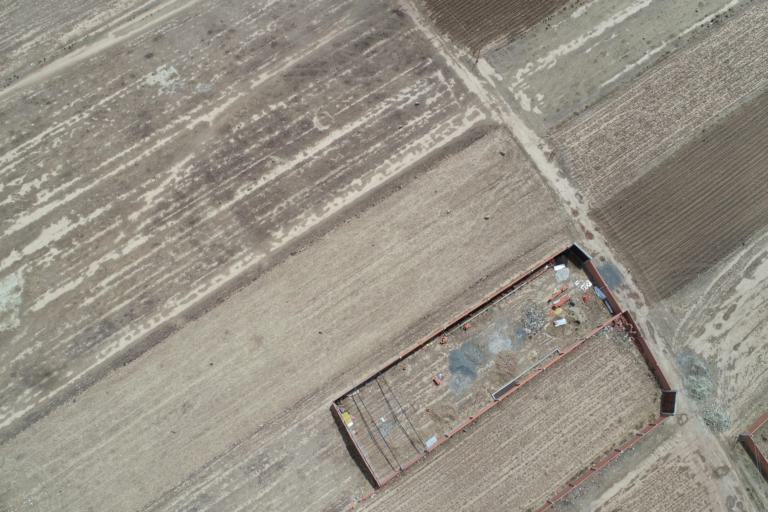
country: BO
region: La Paz
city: Achacachi
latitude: -16.0535
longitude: -68.6772
